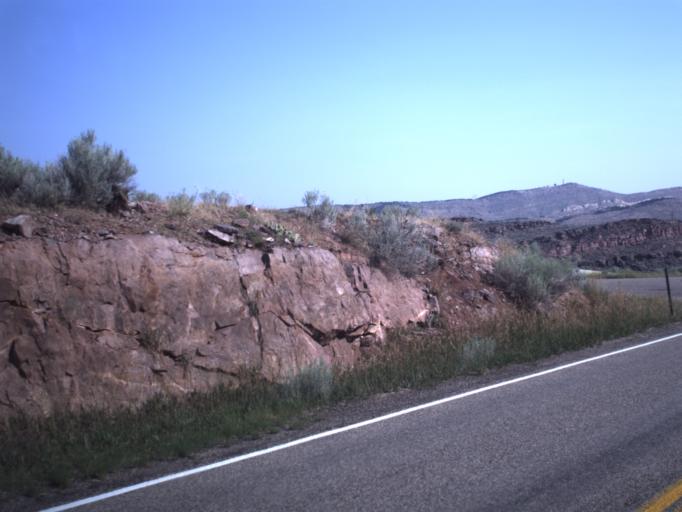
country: US
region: Utah
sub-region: Daggett County
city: Manila
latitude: 40.9238
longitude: -109.4175
